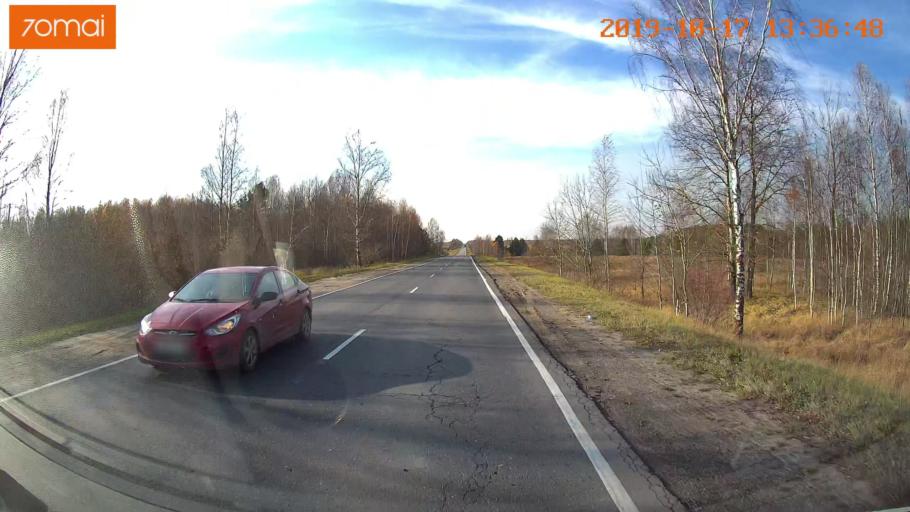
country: RU
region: Rjazan
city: Tuma
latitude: 55.1401
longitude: 40.6546
